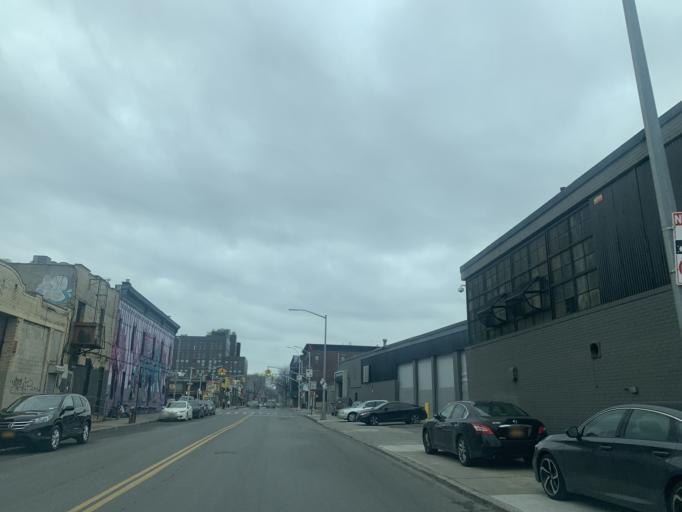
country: US
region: New York
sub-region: Queens County
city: Long Island City
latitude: 40.7080
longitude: -73.9311
